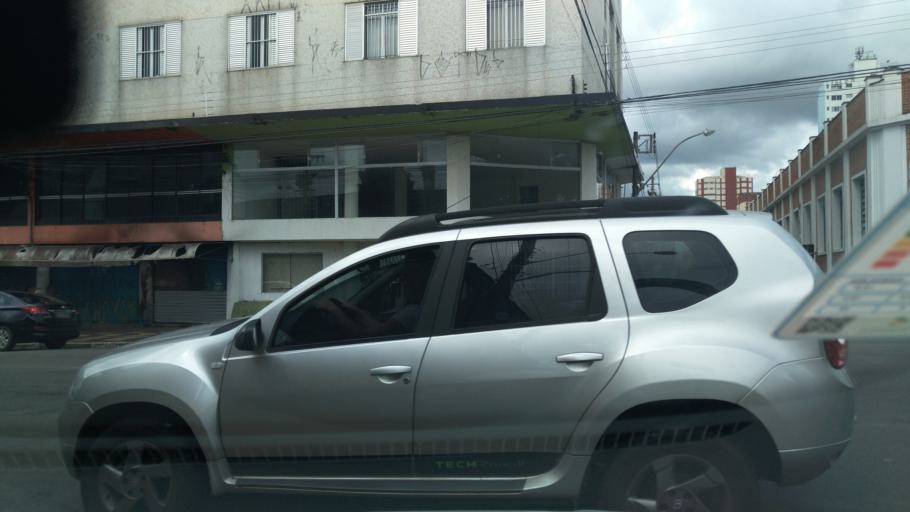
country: BR
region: Sao Paulo
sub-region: Campinas
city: Campinas
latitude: -22.9071
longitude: -47.0677
